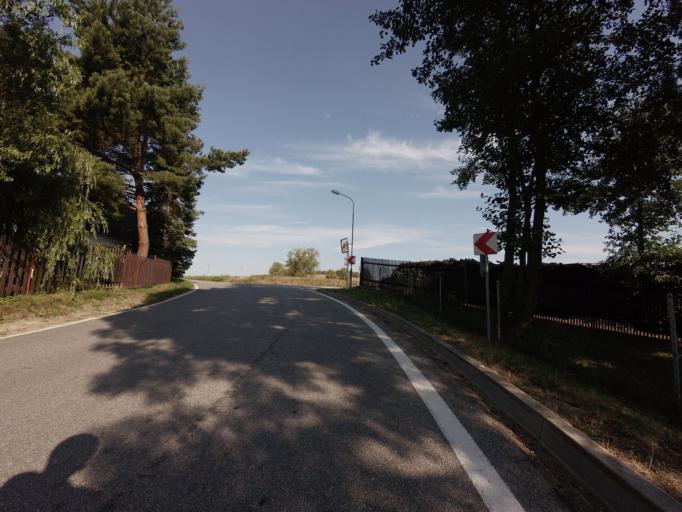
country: CZ
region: Jihocesky
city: Tyn nad Vltavou
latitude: 49.2812
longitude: 14.3976
